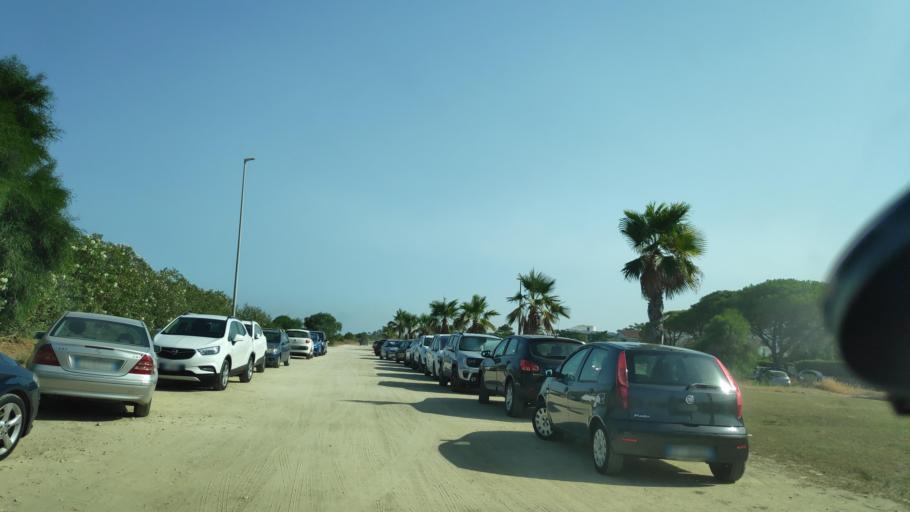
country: IT
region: Calabria
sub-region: Provincia di Catanzaro
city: Isca Marina
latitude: 38.6029
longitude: 16.5658
